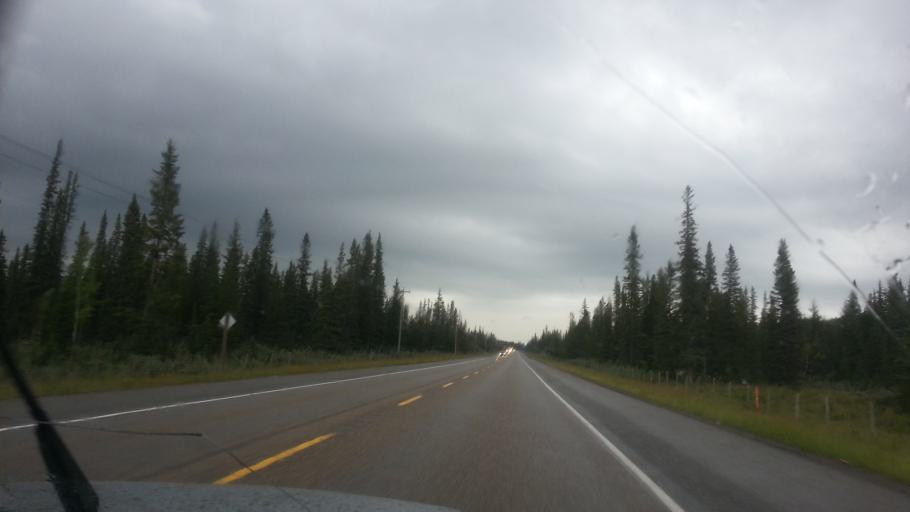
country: CA
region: Alberta
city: Cochrane
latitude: 50.9623
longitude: -114.5484
